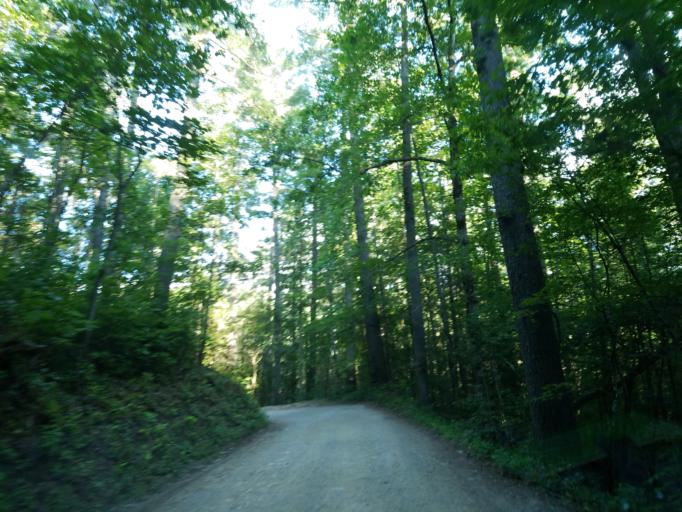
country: US
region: Georgia
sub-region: Union County
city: Blairsville
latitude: 34.7584
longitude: -84.0817
